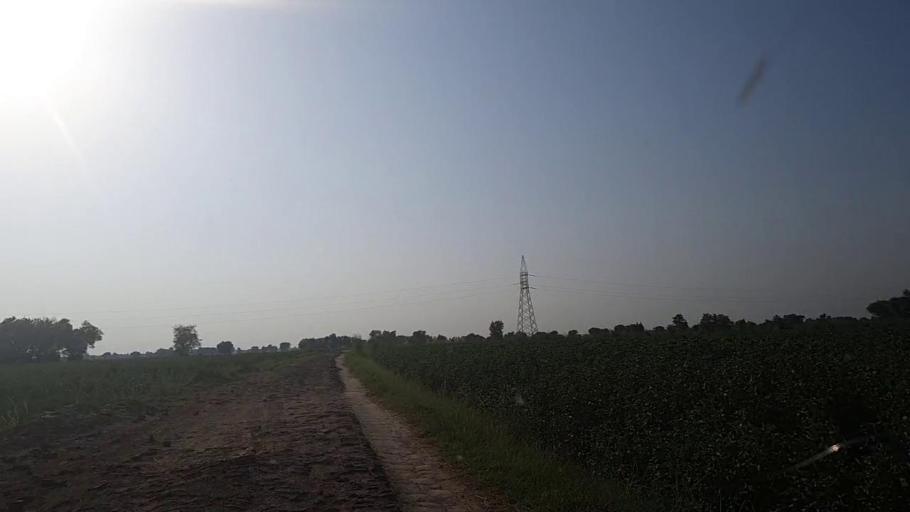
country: PK
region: Sindh
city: Khanpur
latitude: 27.7293
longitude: 69.3060
